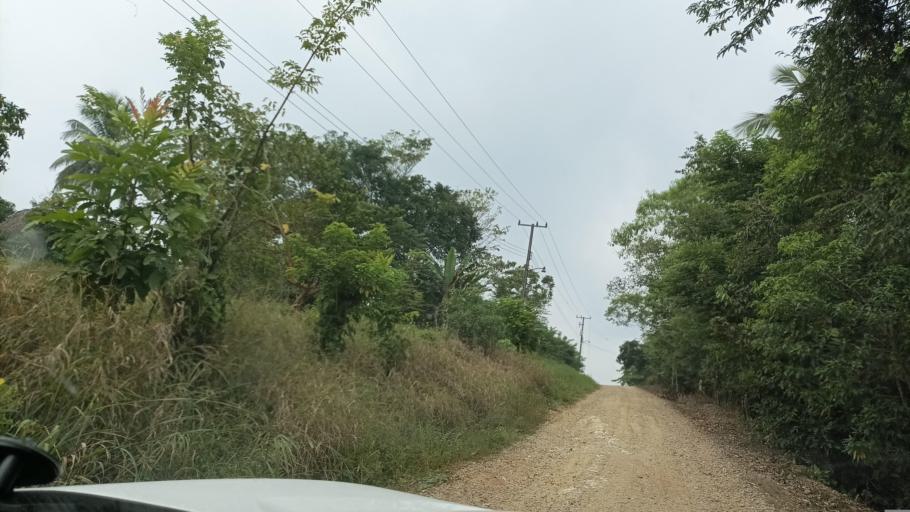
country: MX
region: Veracruz
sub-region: Moloacan
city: Cuichapa
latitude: 17.5768
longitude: -94.2285
